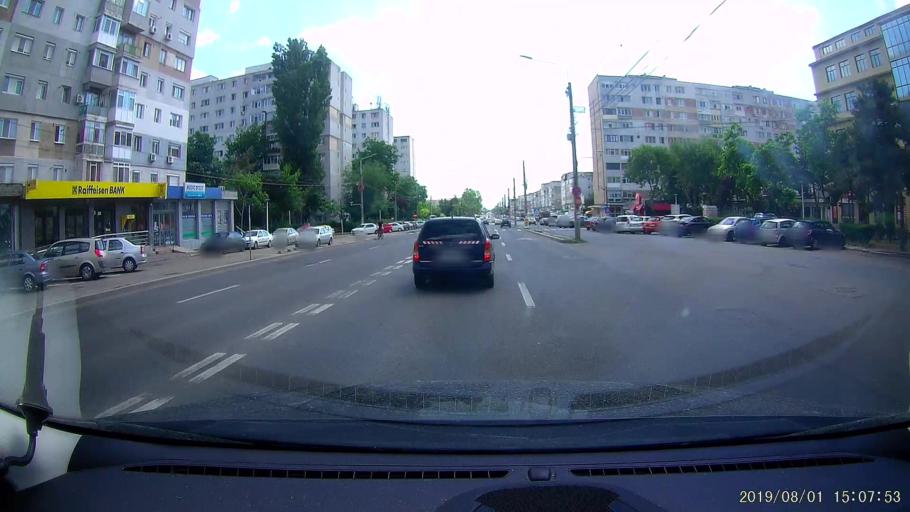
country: RO
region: Braila
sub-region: Municipiul Braila
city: Braila
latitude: 45.2448
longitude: 27.9485
